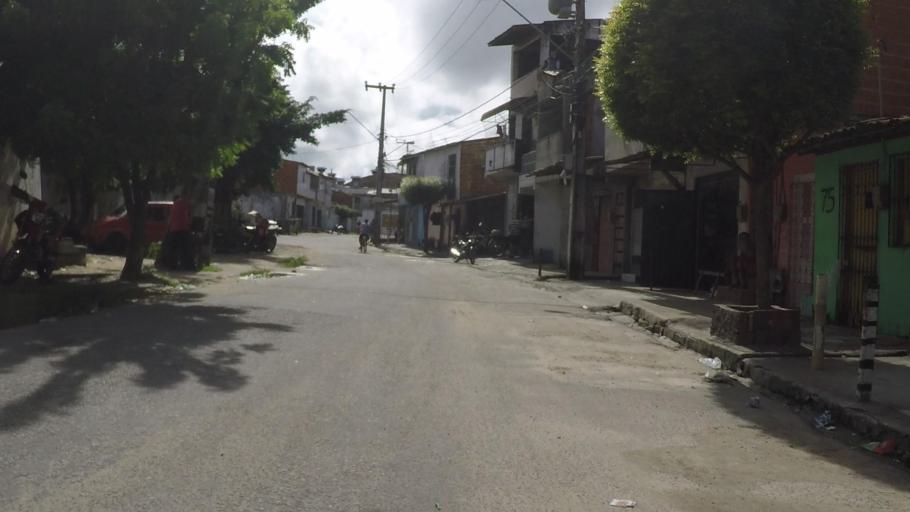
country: BR
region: Ceara
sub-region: Fortaleza
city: Fortaleza
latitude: -3.7399
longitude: -38.5847
